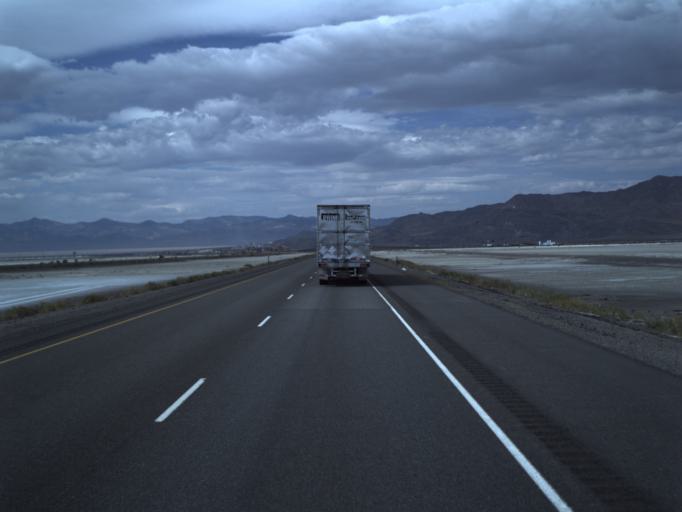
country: US
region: Utah
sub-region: Tooele County
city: Wendover
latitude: 40.7412
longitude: -113.9453
